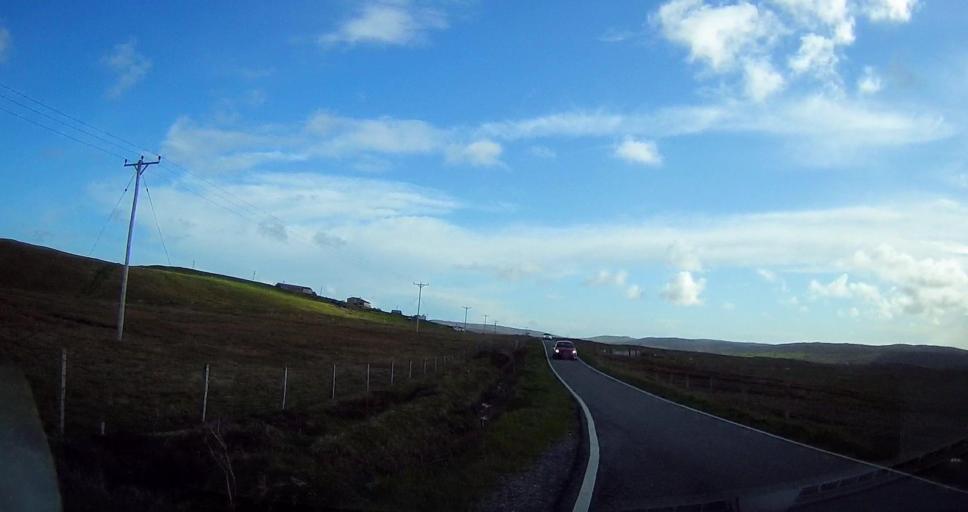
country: GB
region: Scotland
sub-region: Shetland Islands
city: Shetland
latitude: 60.3598
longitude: -1.1441
